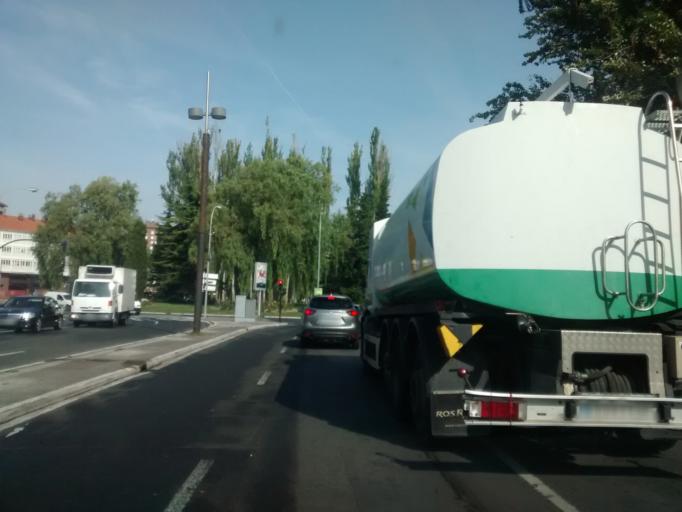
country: ES
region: Basque Country
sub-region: Provincia de Alava
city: Gasteiz / Vitoria
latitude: 42.8581
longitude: -2.6813
